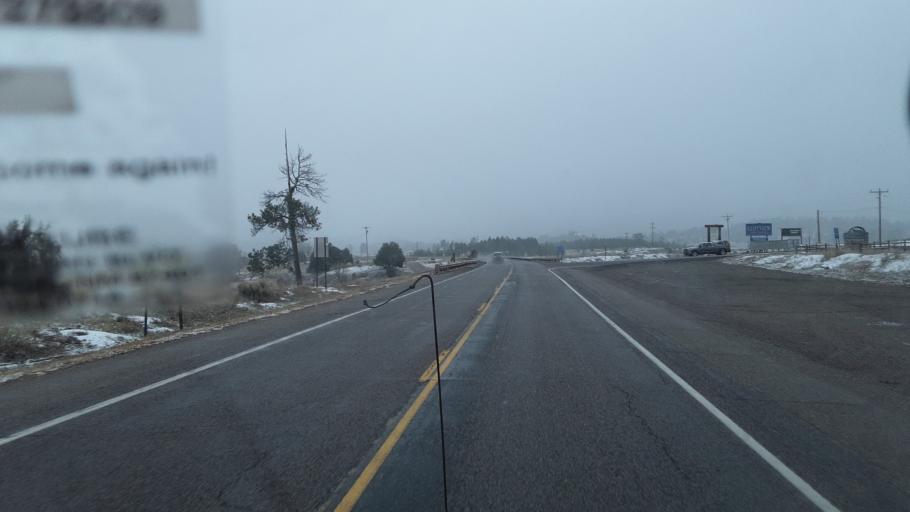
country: US
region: New Mexico
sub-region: Rio Arriba County
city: Tierra Amarilla
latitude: 36.7577
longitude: -106.5594
